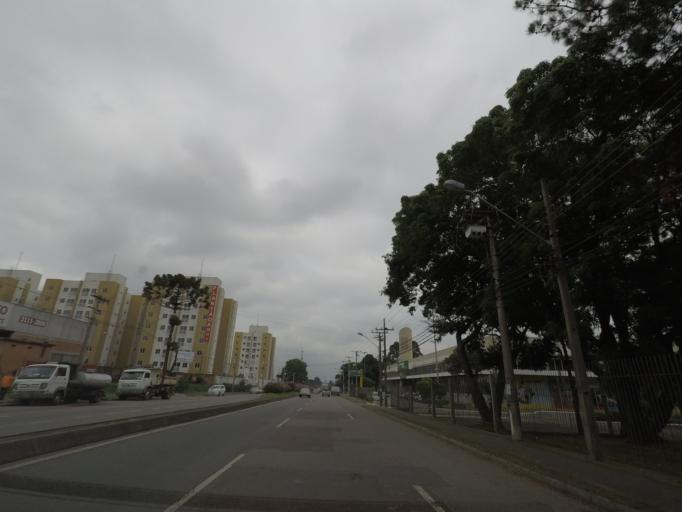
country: BR
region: Parana
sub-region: Curitiba
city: Curitiba
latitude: -25.4954
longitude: -49.3254
